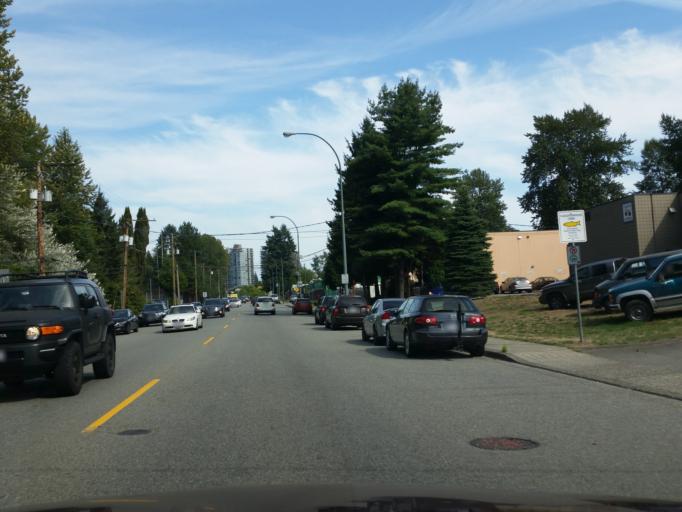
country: CA
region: British Columbia
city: Port Moody
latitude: 49.2788
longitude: -122.8456
